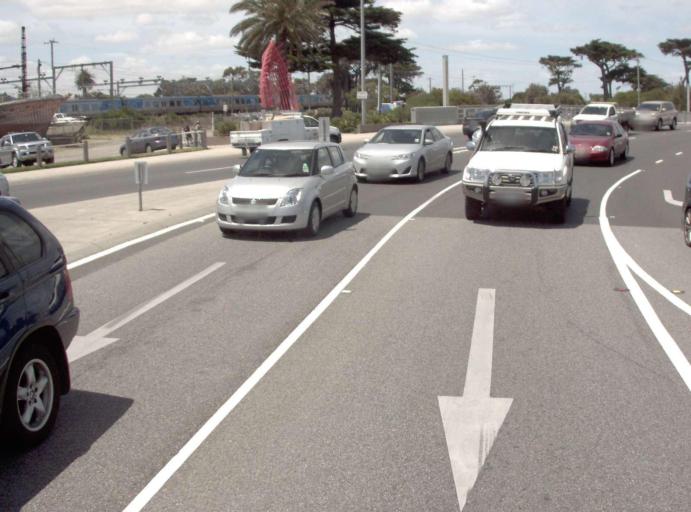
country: AU
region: Victoria
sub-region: Kingston
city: Mordialloc
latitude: -38.0086
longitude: 145.0878
